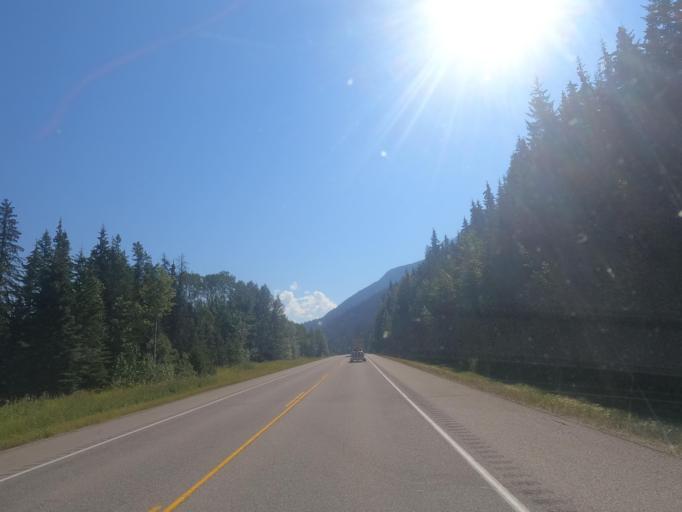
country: CA
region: Alberta
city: Jasper Park Lodge
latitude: 52.8590
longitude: -118.1714
